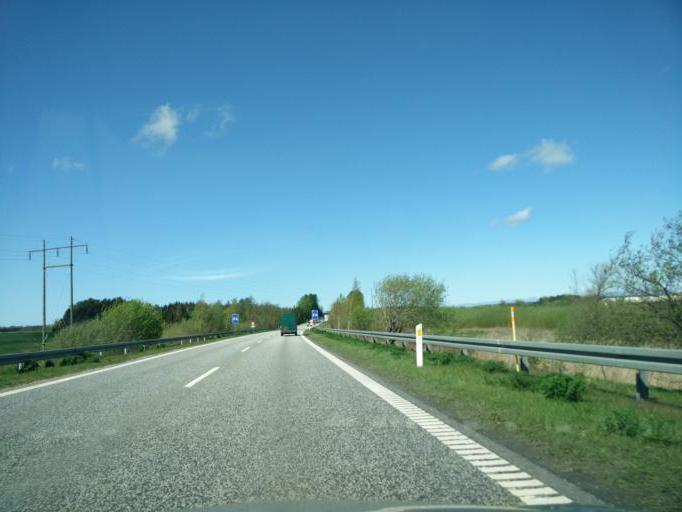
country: DK
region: Capital Region
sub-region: Gribskov Kommune
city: Helsinge
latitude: 56.0015
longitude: 12.2394
